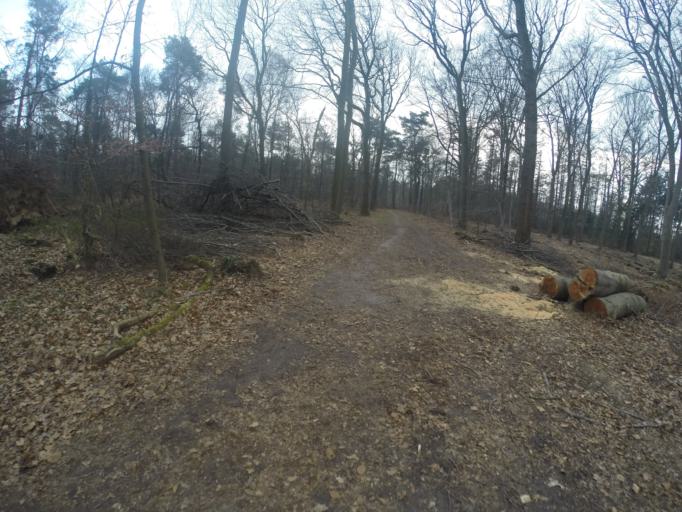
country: NL
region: Gelderland
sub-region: Gemeente Lochem
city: Almen
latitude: 52.1306
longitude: 6.2822
